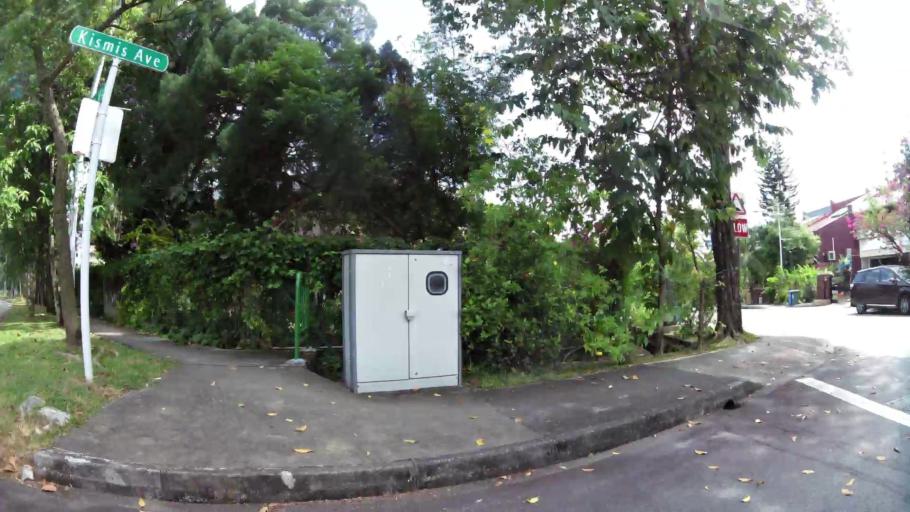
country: SG
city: Singapore
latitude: 1.3351
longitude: 103.7712
